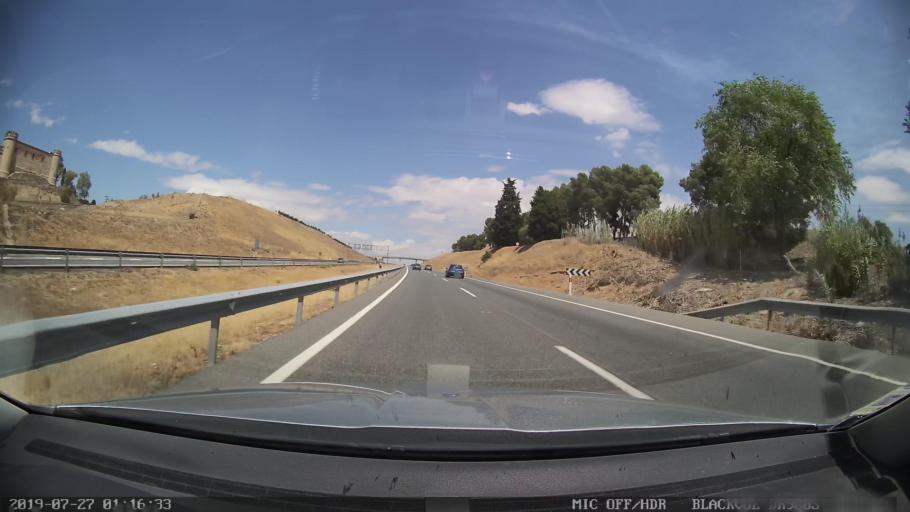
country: ES
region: Castille-La Mancha
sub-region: Province of Toledo
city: Maqueda
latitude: 40.0635
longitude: -4.3677
